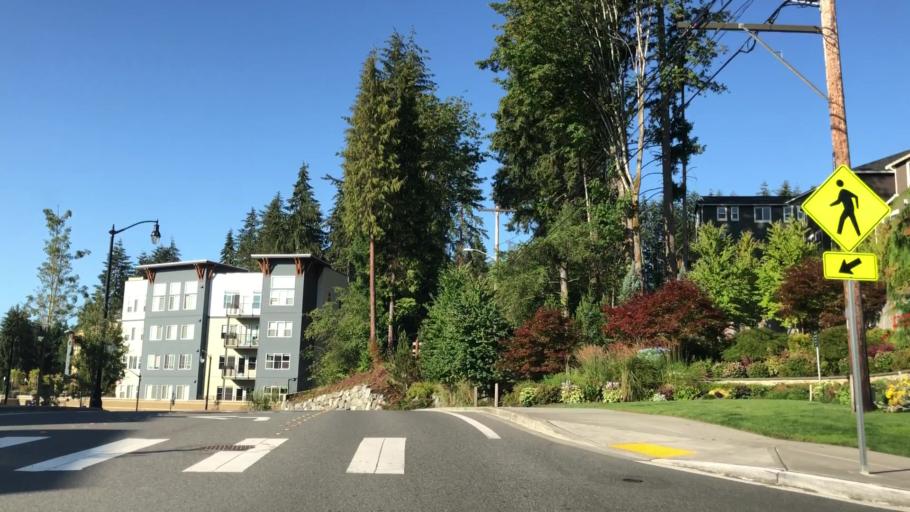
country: US
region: Washington
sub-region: King County
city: Bothell
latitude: 47.7675
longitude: -122.1923
